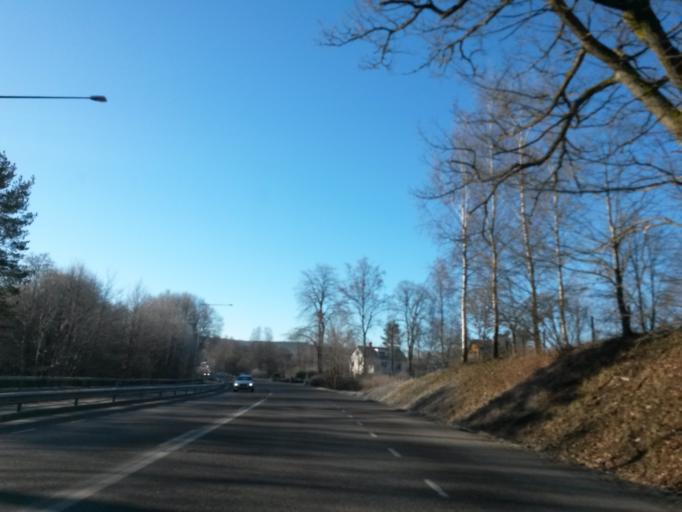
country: SE
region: Vaestra Goetaland
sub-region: Boras Kommun
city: Ganghester
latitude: 57.8087
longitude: 13.0115
